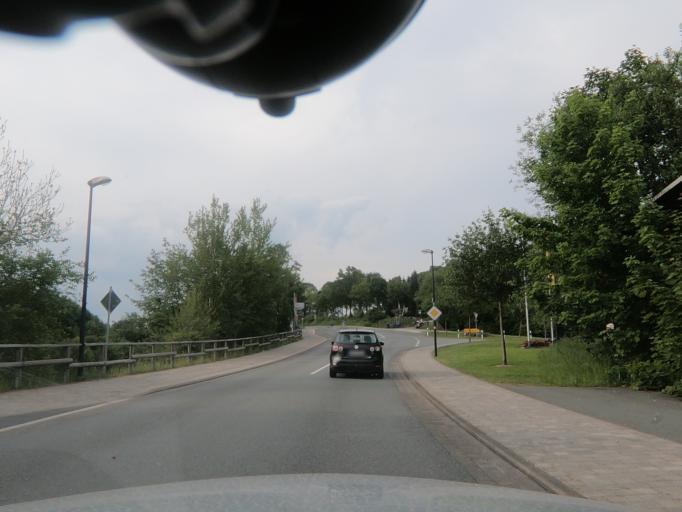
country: DE
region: North Rhine-Westphalia
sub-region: Regierungsbezirk Arnsberg
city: Winterberg
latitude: 51.2016
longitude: 8.5339
